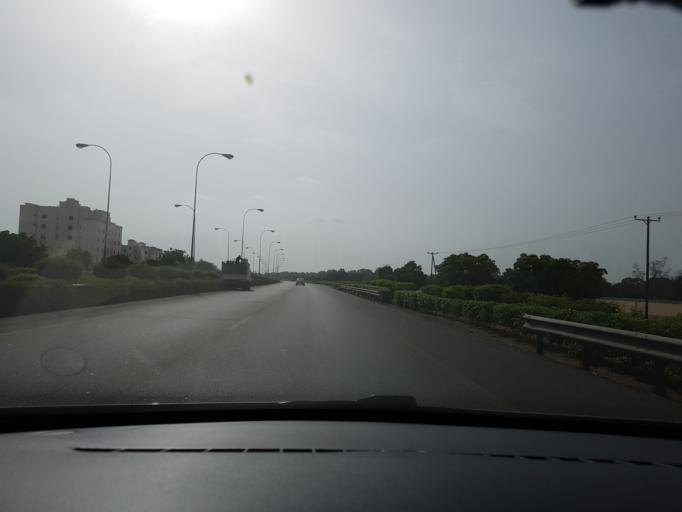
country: OM
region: Al Batinah
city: Al Sohar
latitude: 24.3964
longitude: 56.6731
